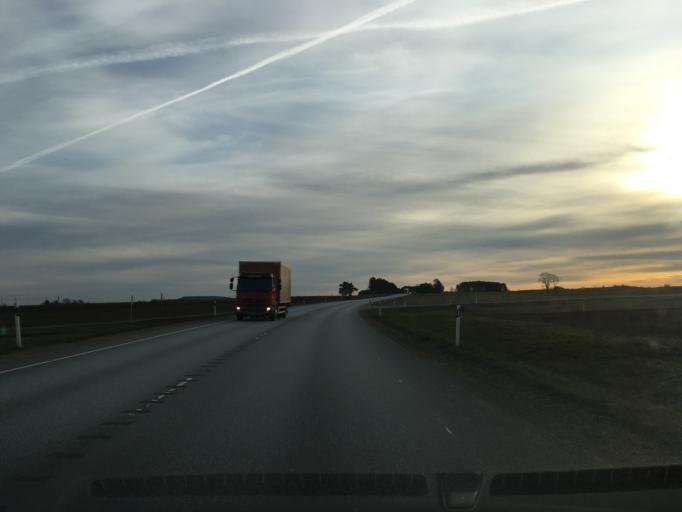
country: EE
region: Ida-Virumaa
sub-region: Puessi linn
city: Pussi
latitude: 59.4116
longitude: 27.0446
